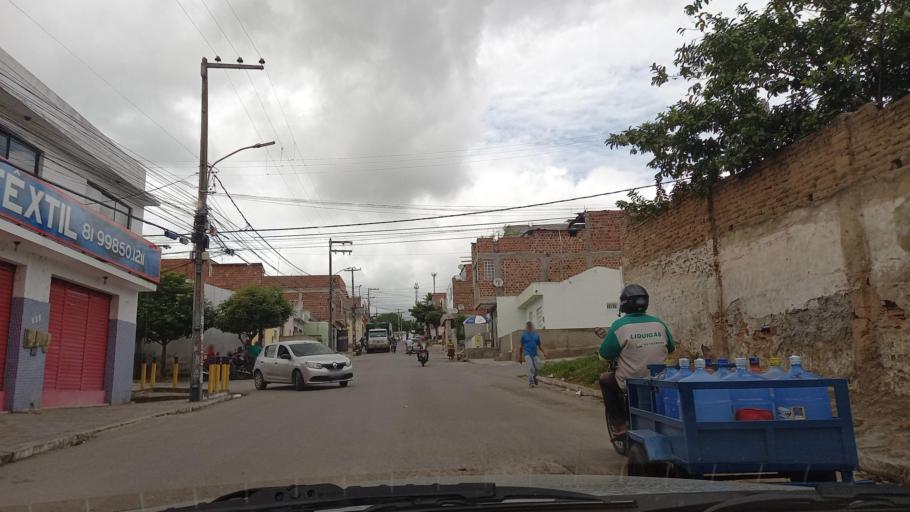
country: BR
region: Pernambuco
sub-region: Caruaru
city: Caruaru
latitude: -8.2739
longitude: -35.9572
